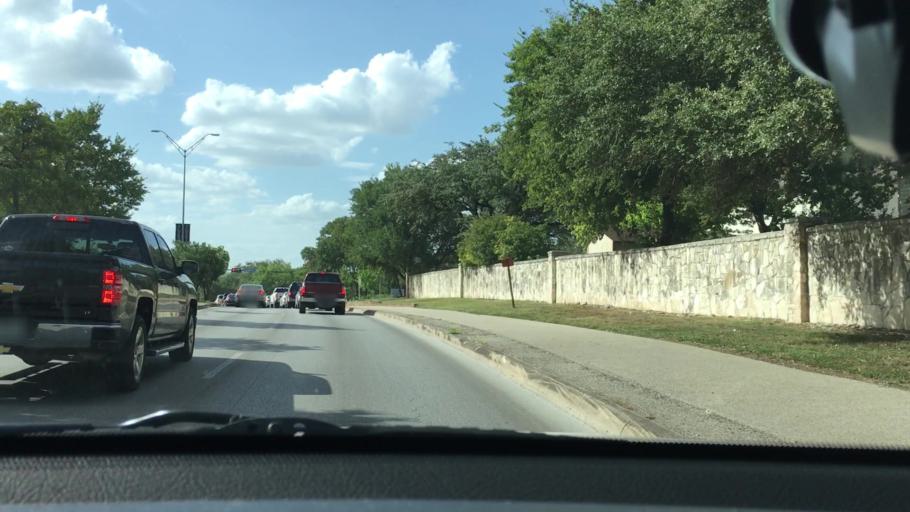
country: US
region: Texas
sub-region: Bexar County
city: Selma
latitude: 29.5810
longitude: -98.2816
